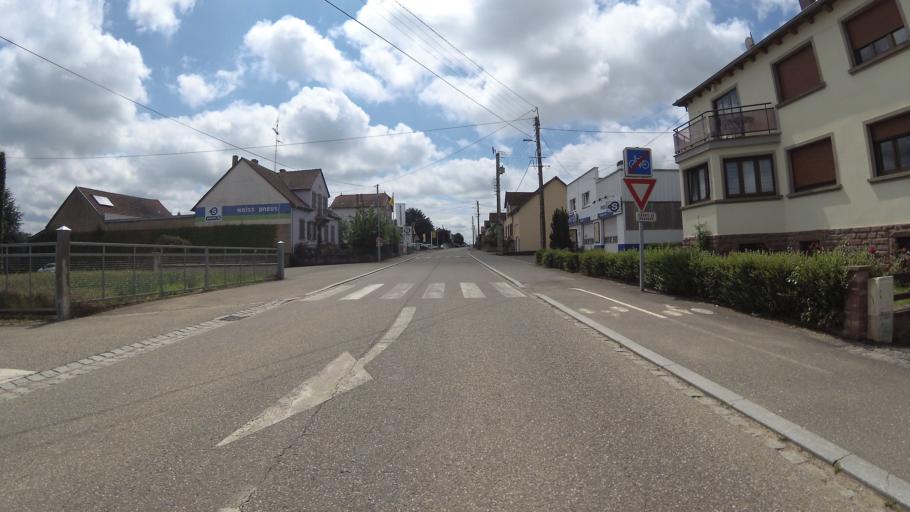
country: FR
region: Alsace
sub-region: Departement du Bas-Rhin
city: Diemeringen
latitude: 48.9476
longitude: 7.1856
